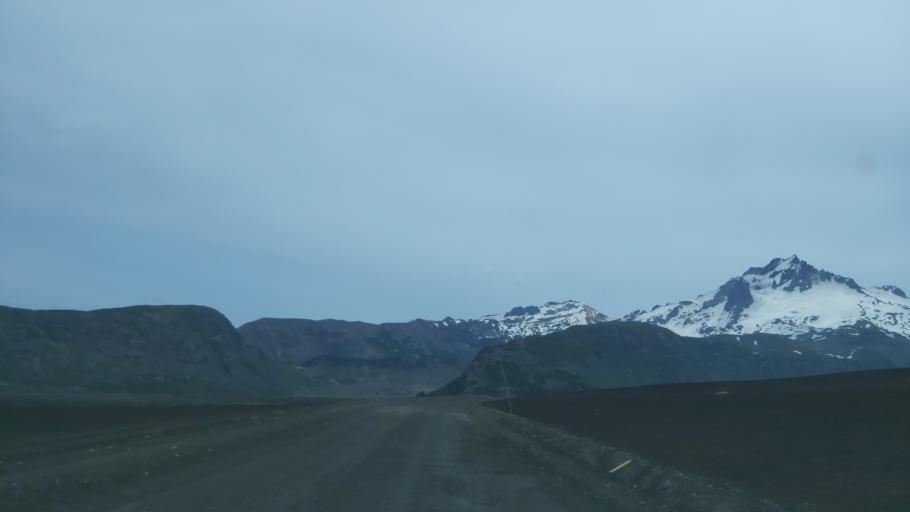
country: AR
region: Neuquen
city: Andacollo
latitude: -37.4567
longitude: -71.2965
